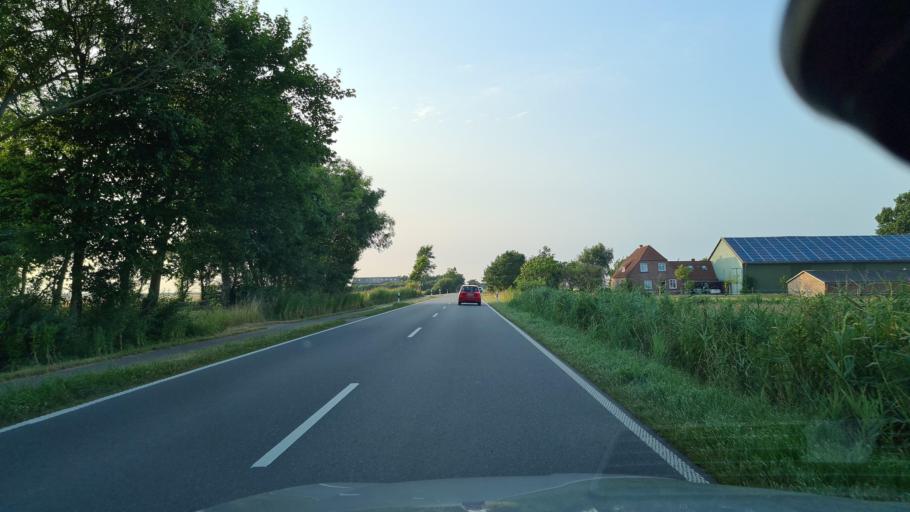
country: DE
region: Schleswig-Holstein
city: Elisabeth-Sophien-Koog
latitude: 54.5093
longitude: 8.9362
